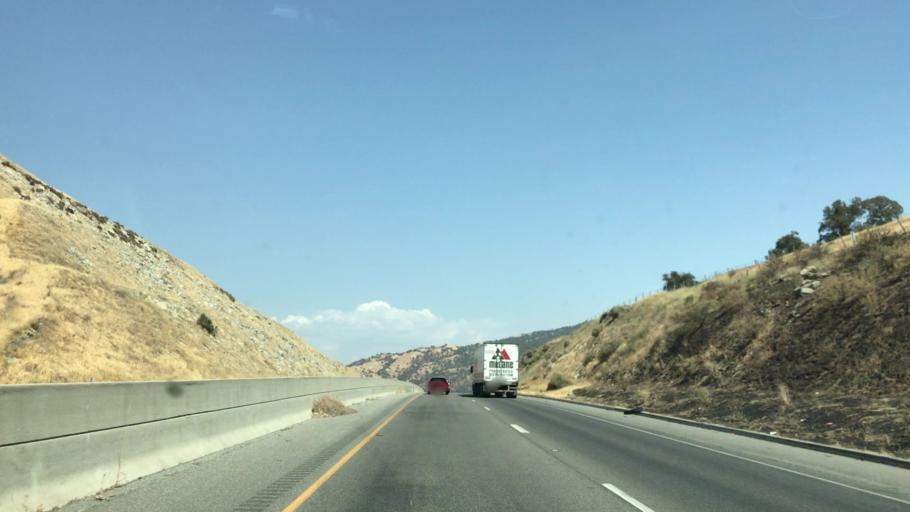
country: US
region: California
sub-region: Kern County
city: Bear Valley Springs
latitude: 35.2692
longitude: -118.6767
